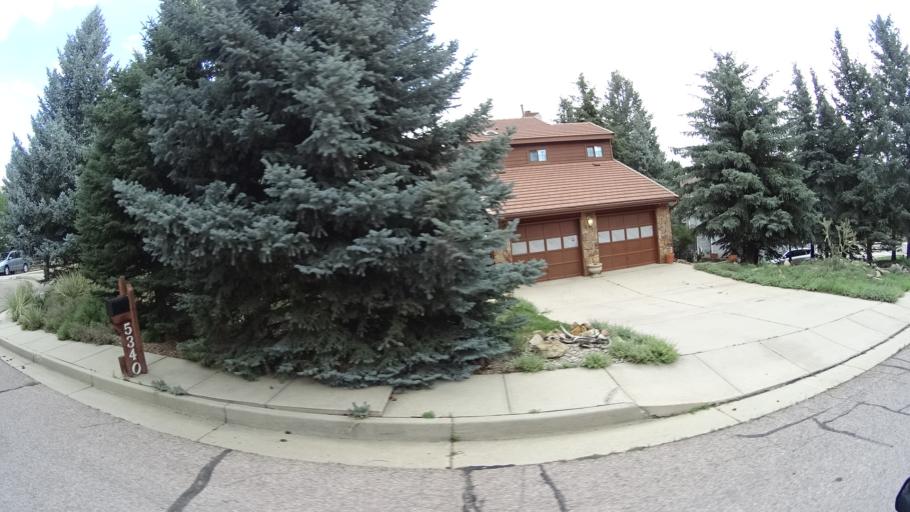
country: US
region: Colorado
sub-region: El Paso County
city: Colorado Springs
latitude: 38.9090
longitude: -104.8475
